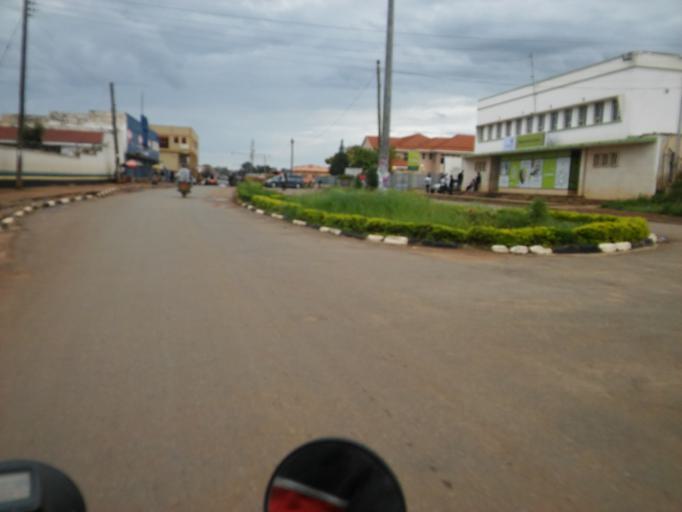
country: UG
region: Eastern Region
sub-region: Mbale District
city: Mbale
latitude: 1.0699
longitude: 34.1804
